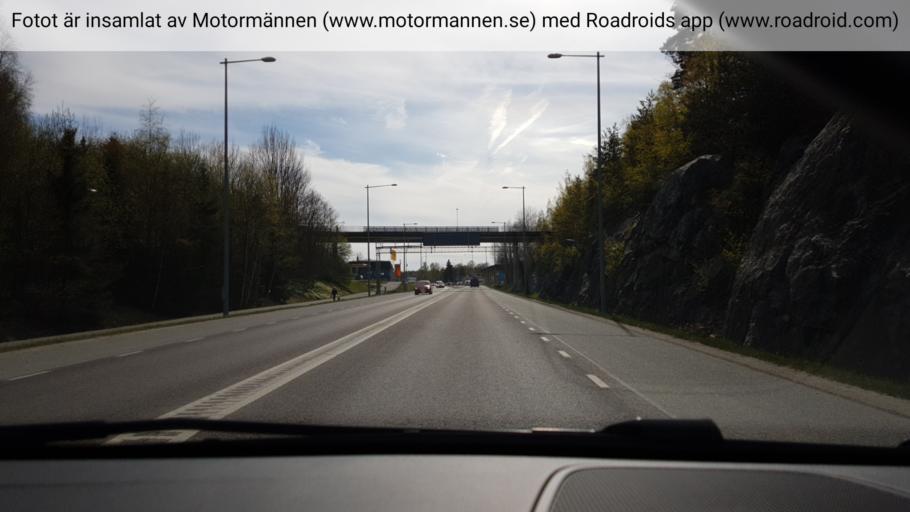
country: SE
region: Stockholm
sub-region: Botkyrka Kommun
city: Tumba
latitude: 59.1971
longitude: 17.8343
